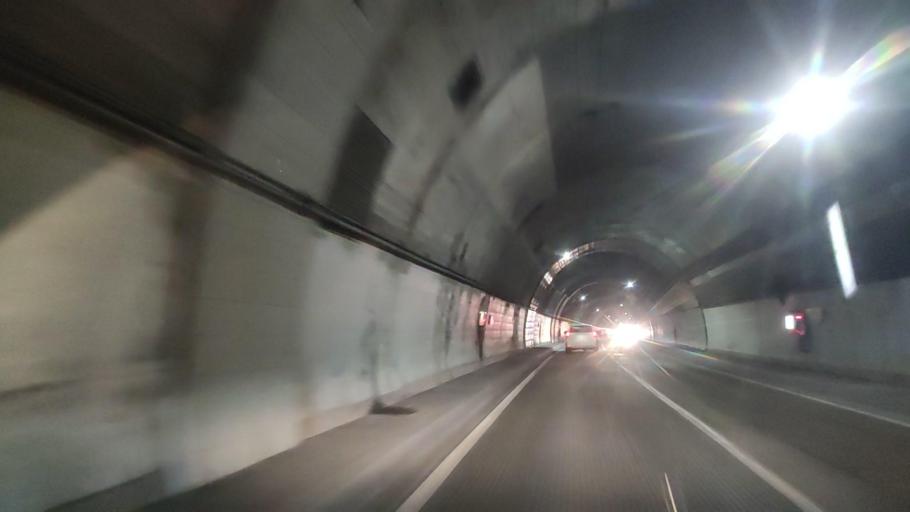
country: JP
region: Hokkaido
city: Ishikari
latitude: 43.4436
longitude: 141.4133
